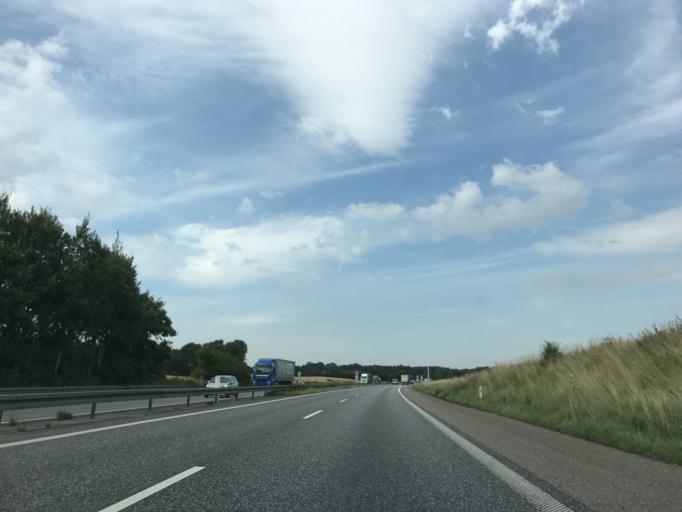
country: DK
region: South Denmark
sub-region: Haderslev Kommune
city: Vojens
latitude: 55.2088
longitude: 9.3719
